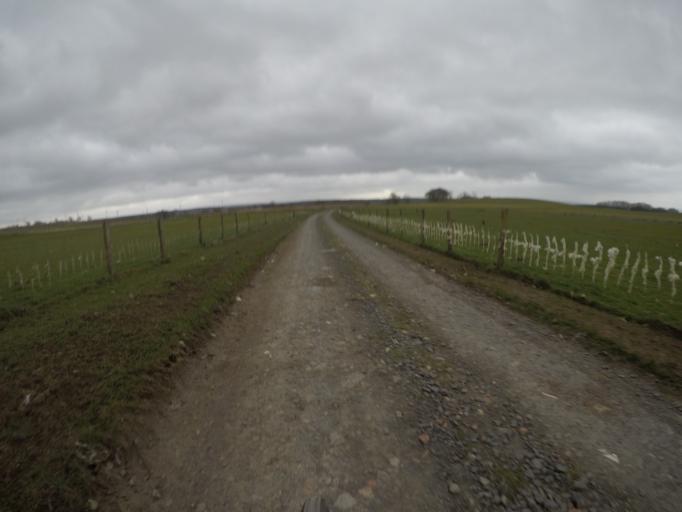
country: GB
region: Scotland
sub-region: East Ayrshire
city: Galston
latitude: 55.6715
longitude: -4.3733
